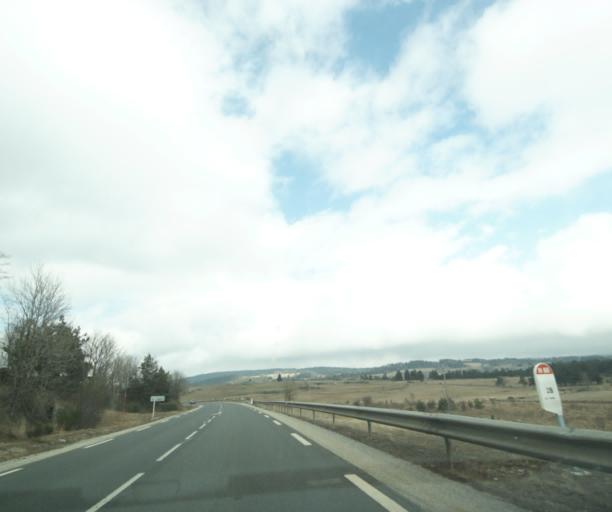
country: FR
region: Languedoc-Roussillon
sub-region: Departement de la Lozere
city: Mende
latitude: 44.5907
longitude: 3.6691
